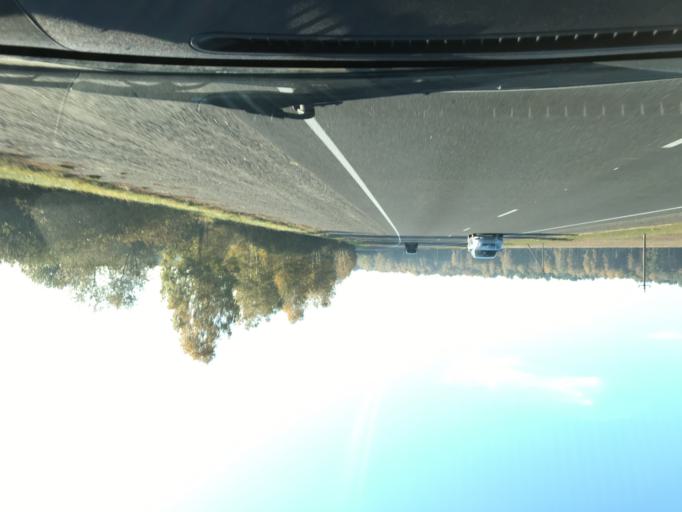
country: BY
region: Brest
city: Asnyezhytsy
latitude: 52.2270
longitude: 26.1400
